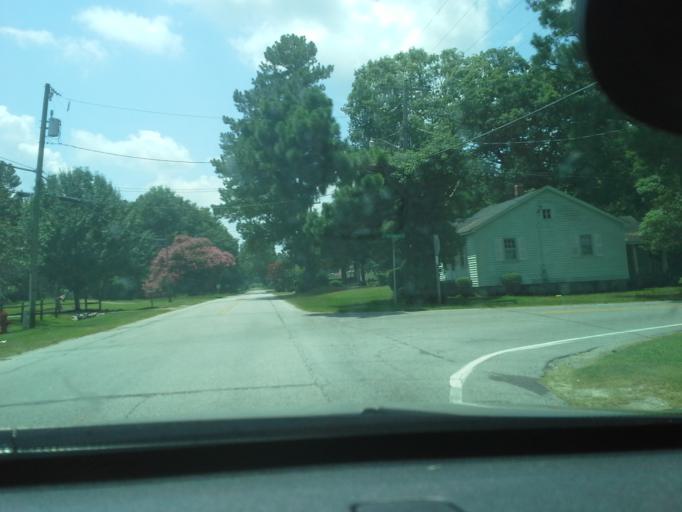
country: US
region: North Carolina
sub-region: Washington County
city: Plymouth
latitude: 35.8511
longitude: -76.7580
